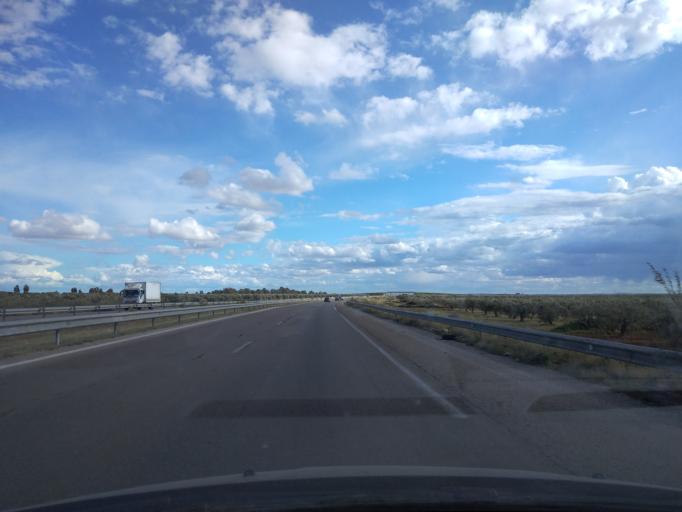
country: TN
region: Al Munastir
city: Manzil Kamil
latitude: 35.6272
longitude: 10.5913
